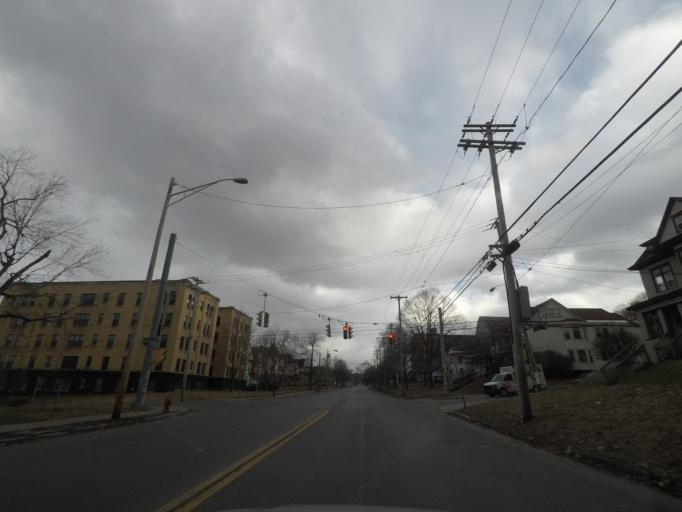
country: US
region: New York
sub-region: Onondaga County
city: Syracuse
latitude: 43.0469
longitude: -76.1280
